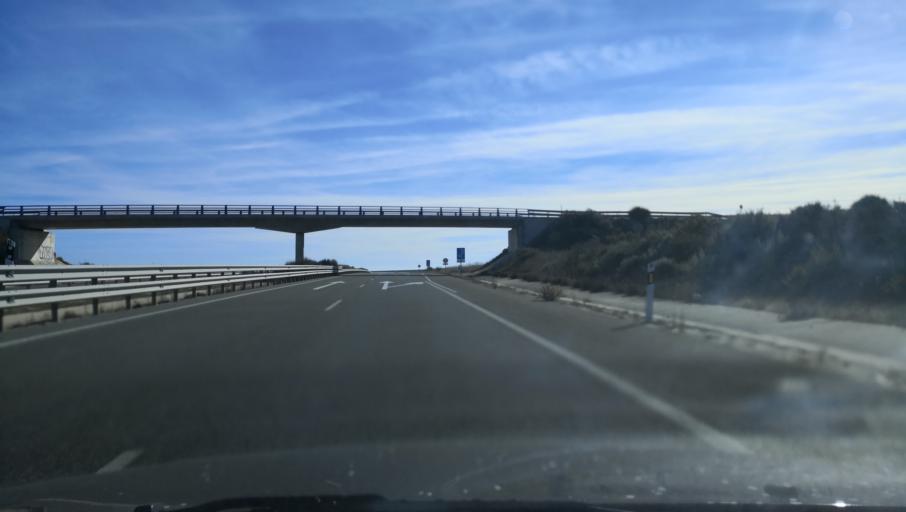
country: ES
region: Castille and Leon
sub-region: Provincia de Salamanca
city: Cantaracillo
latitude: 40.8918
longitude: -5.1568
